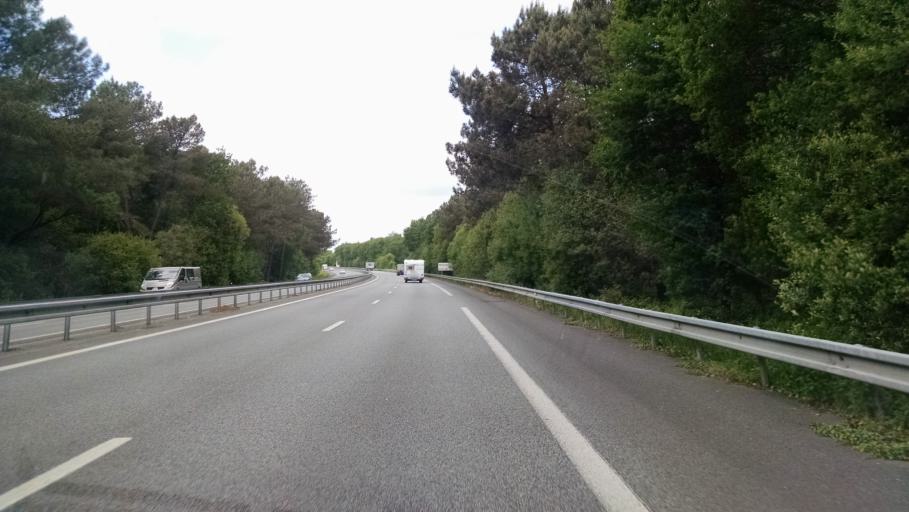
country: FR
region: Brittany
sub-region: Departement du Morbihan
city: Landevant
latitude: 47.7513
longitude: -3.1081
